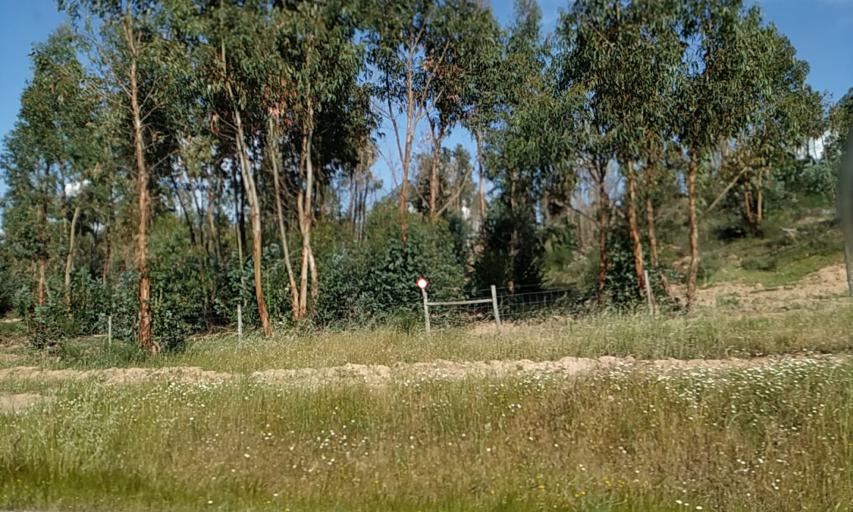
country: PT
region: Portalegre
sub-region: Fronteira
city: Fronteira
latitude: 38.9996
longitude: -7.4688
